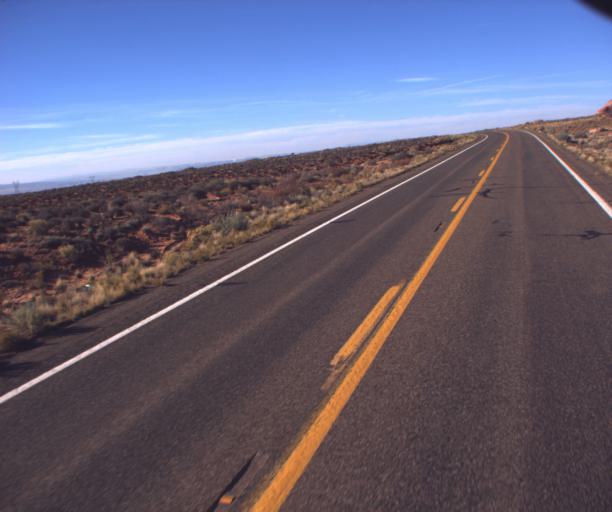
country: US
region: Arizona
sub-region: Coconino County
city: LeChee
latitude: 36.8253
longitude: -111.3092
